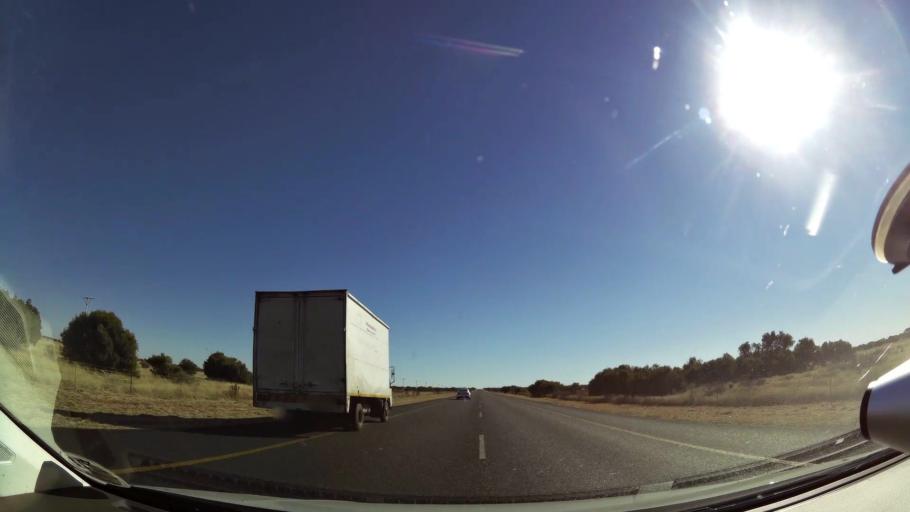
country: ZA
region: Northern Cape
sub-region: Frances Baard District Municipality
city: Warrenton
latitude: -28.2205
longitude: 24.8487
